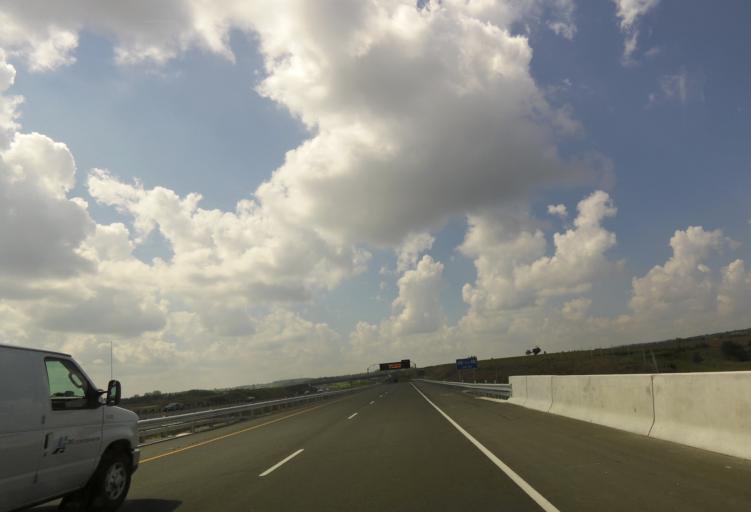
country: CA
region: Ontario
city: Ajax
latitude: 43.9505
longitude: -78.9785
